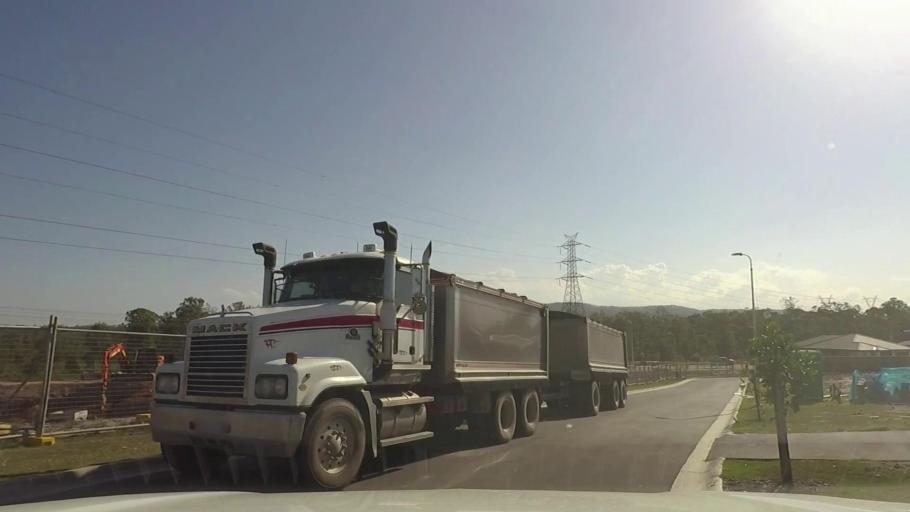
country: AU
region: Queensland
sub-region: Logan
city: Chambers Flat
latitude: -27.8184
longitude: 153.1296
